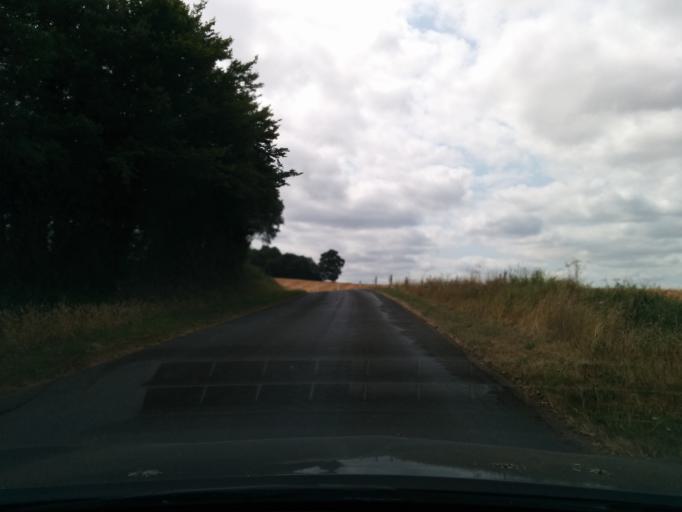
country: FR
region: Centre
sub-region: Departement du Cher
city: Sancerre
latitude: 47.3257
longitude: 2.7492
